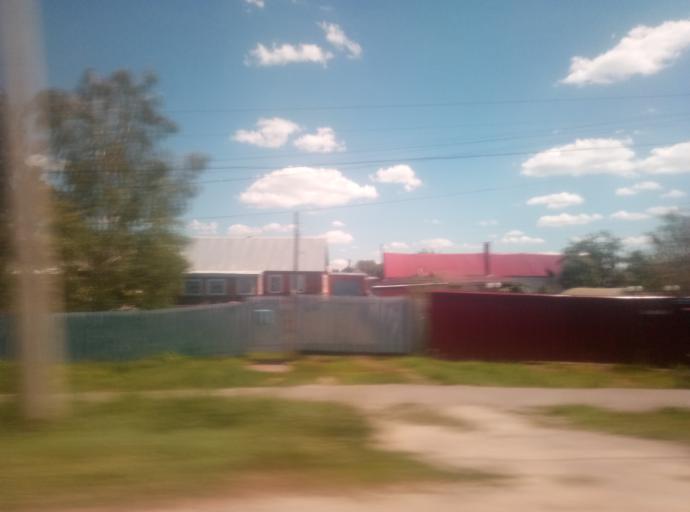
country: RU
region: Tula
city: Kireyevsk
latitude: 53.9847
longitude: 37.9329
